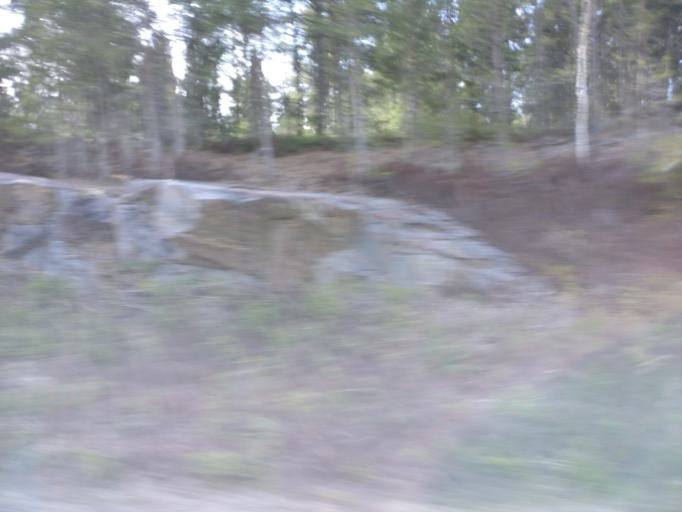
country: FI
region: Uusimaa
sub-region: Raaseporin
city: Inga
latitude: 60.0741
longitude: 23.9549
